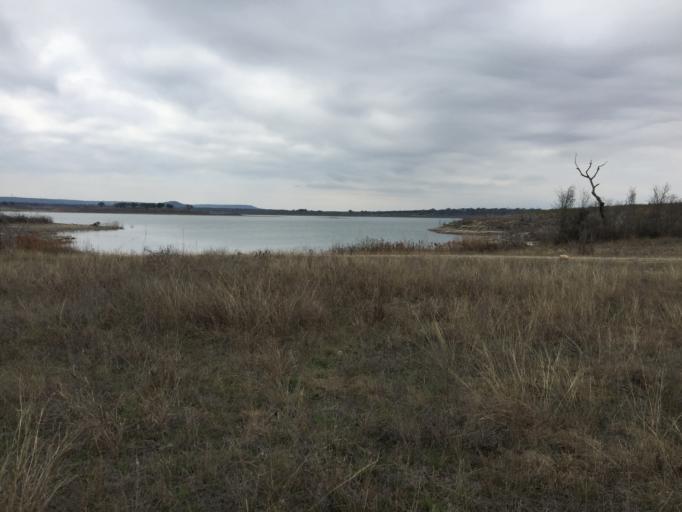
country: US
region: Texas
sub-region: Bell County
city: Nolanville
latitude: 31.0265
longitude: -97.6172
